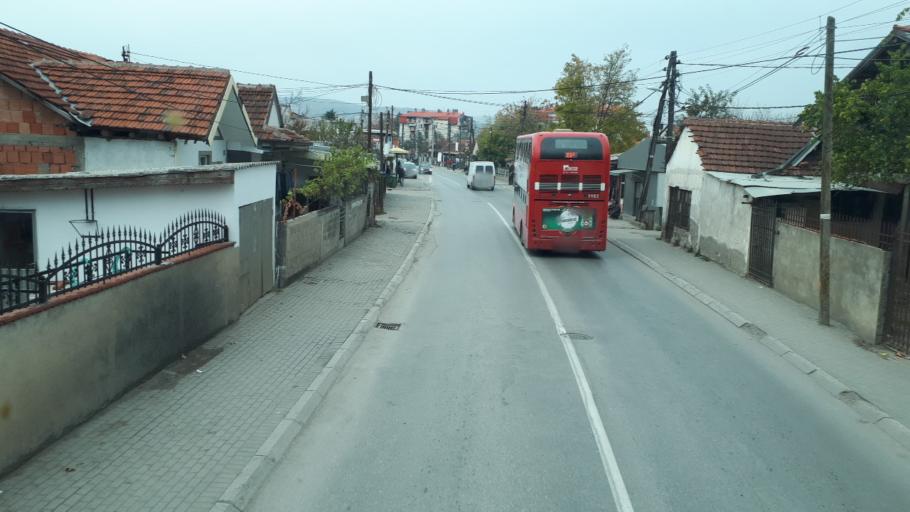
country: MK
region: Saraj
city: Saraj
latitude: 42.0155
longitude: 21.3581
